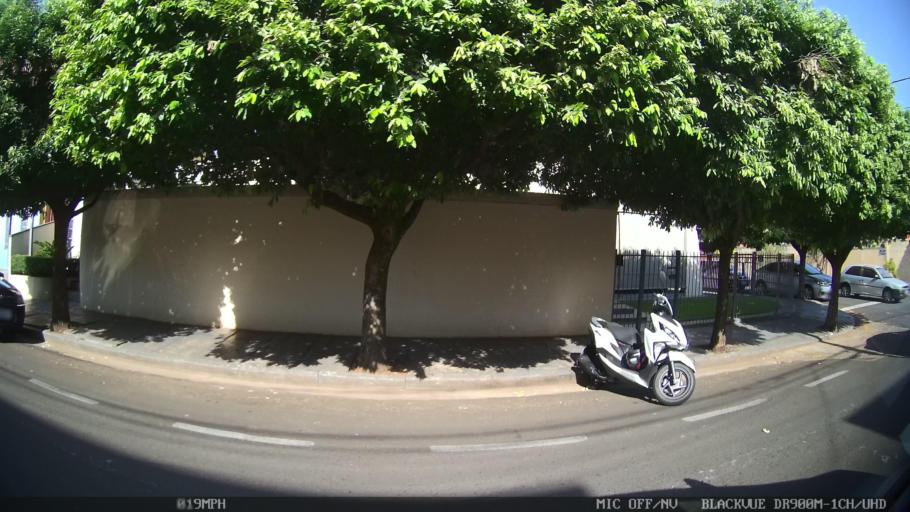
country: BR
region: Sao Paulo
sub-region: Sao Jose Do Rio Preto
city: Sao Jose do Rio Preto
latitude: -20.8070
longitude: -49.3964
